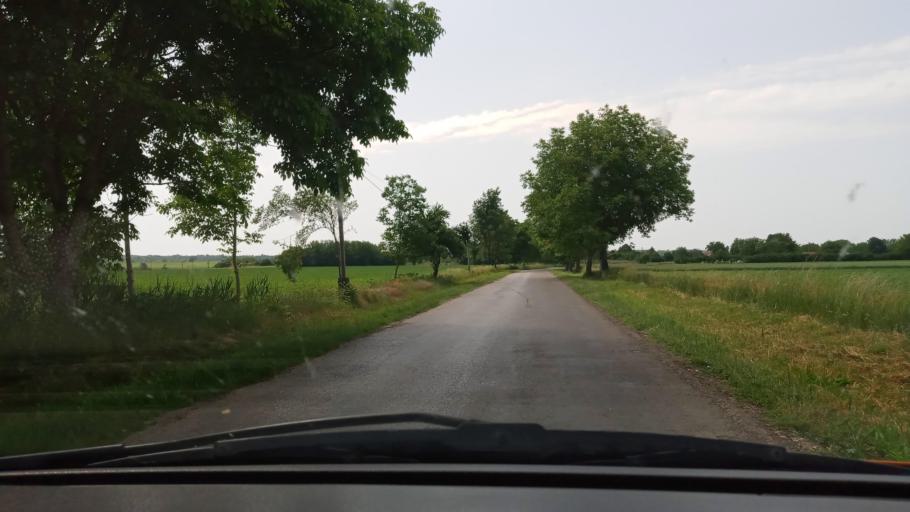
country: HU
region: Baranya
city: Szentlorinc
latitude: 45.9968
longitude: 18.0368
